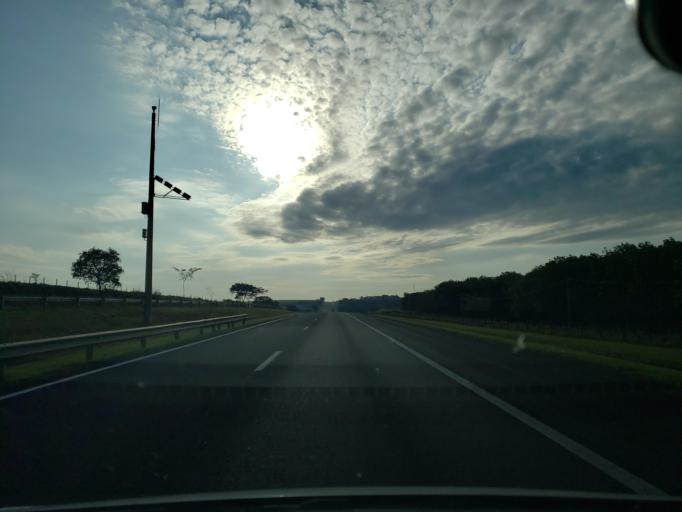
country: BR
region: Sao Paulo
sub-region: Valparaiso
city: Valparaiso
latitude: -21.1709
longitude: -50.9331
